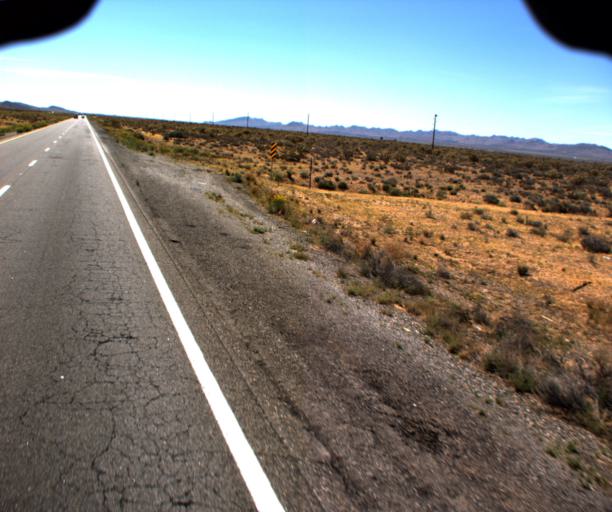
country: US
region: Arizona
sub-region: Mohave County
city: Dolan Springs
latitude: 35.5114
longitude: -114.3400
